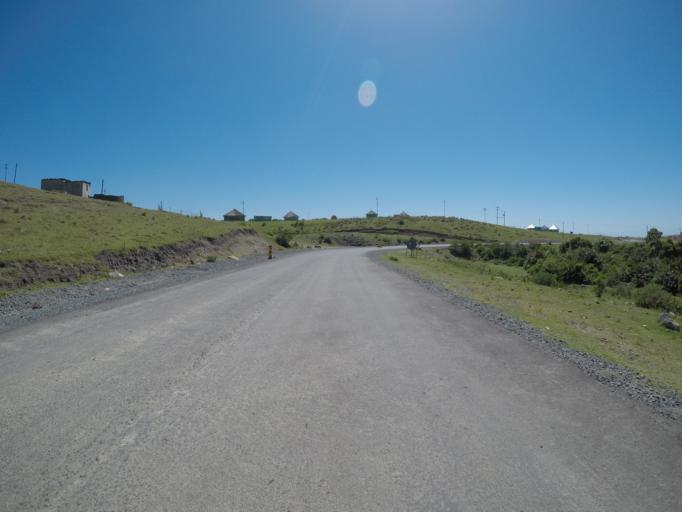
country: ZA
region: Eastern Cape
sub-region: OR Tambo District Municipality
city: Libode
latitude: -31.9993
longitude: 29.1202
